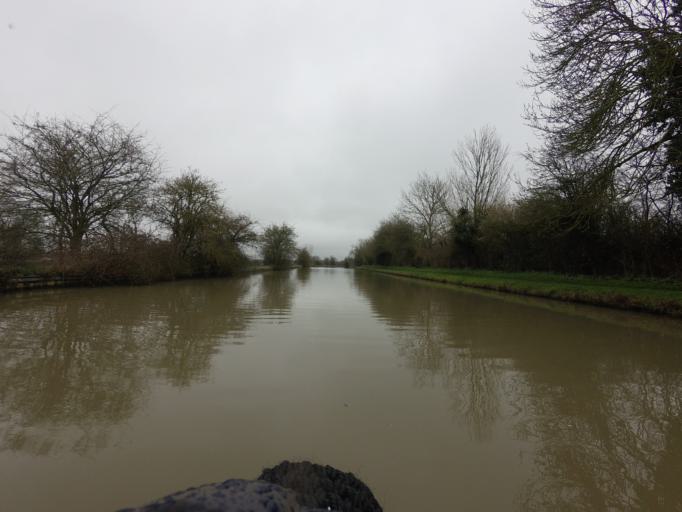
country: GB
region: England
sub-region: Milton Keynes
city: Castlethorpe
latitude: 52.0797
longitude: -0.8449
